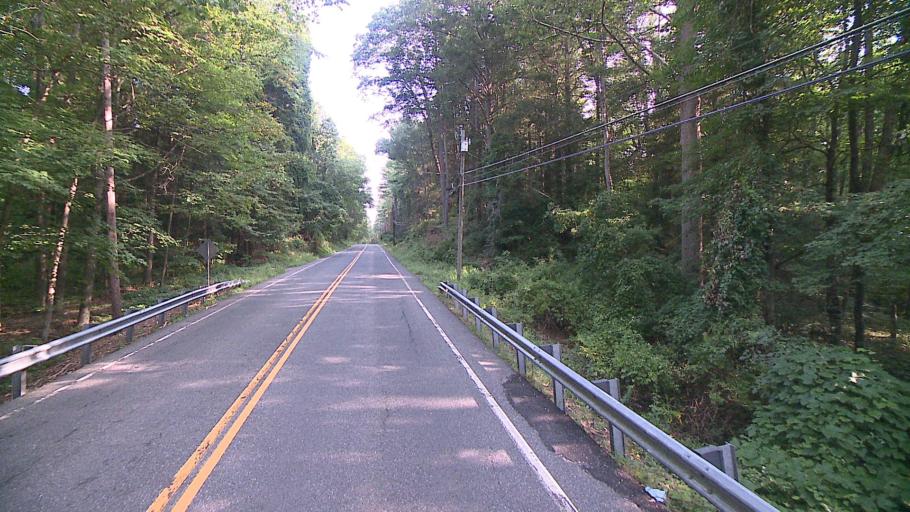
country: US
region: Connecticut
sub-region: Litchfield County
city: Canaan
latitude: 41.9061
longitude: -73.3653
